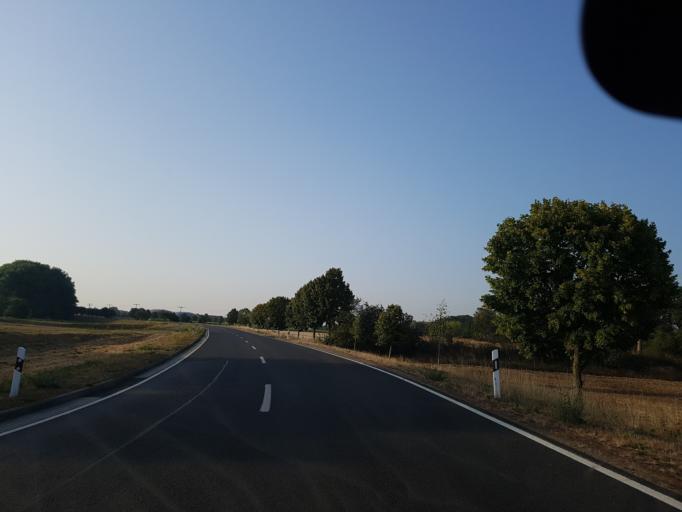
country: DE
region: Brandenburg
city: Muhlberg
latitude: 51.4116
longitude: 13.1817
